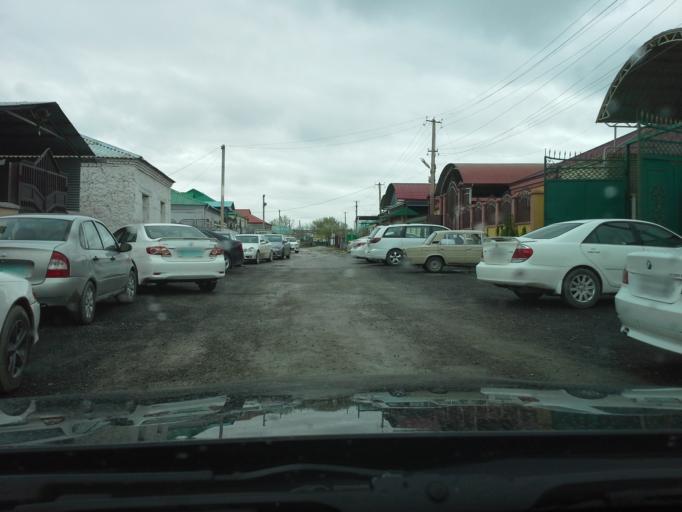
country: TM
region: Ahal
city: Abadan
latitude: 37.9663
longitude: 58.2122
